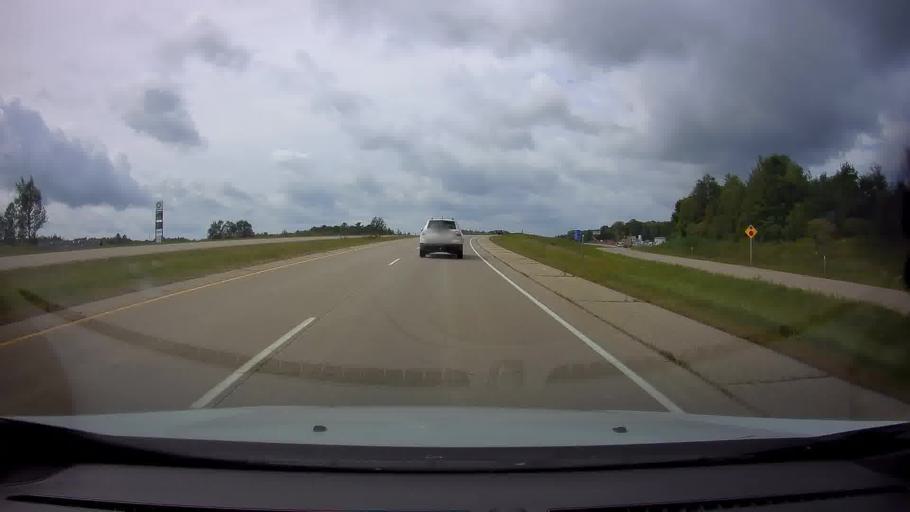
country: US
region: Wisconsin
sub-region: Shawano County
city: Wittenberg
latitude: 44.8246
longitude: -89.1193
